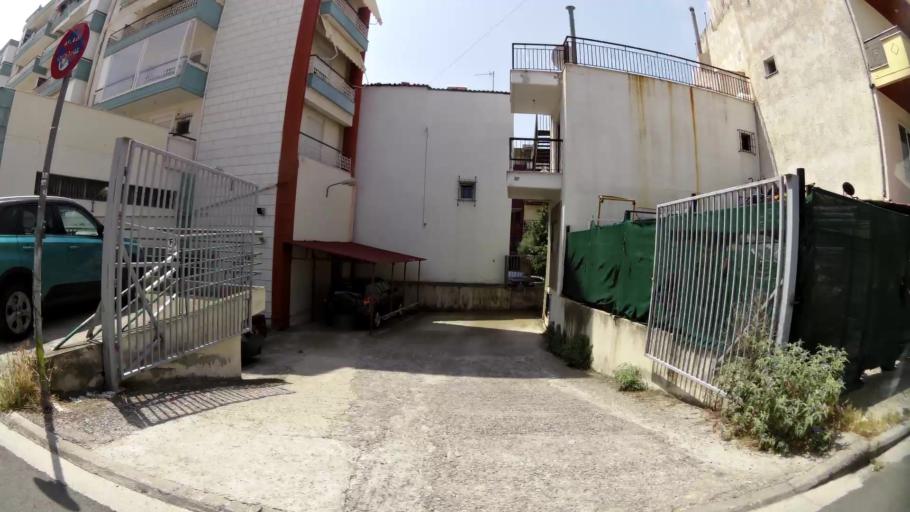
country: GR
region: Central Macedonia
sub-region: Nomos Thessalonikis
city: Evosmos
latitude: 40.6741
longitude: 22.9063
